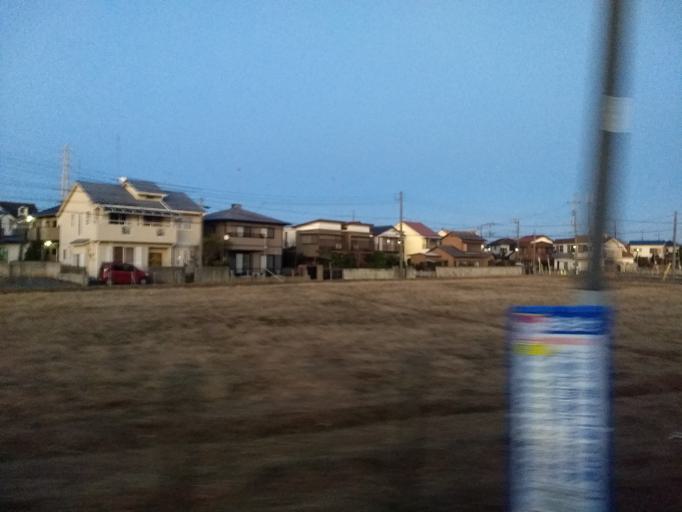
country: JP
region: Chiba
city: Kashiwa
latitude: 35.8678
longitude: 139.9569
